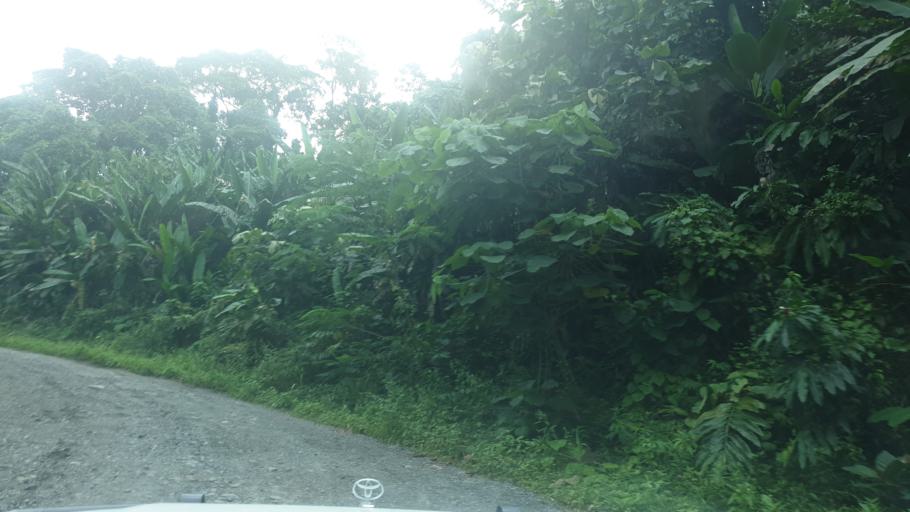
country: PG
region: Bougainville
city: Panguna
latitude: -6.6199
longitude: 155.7675
